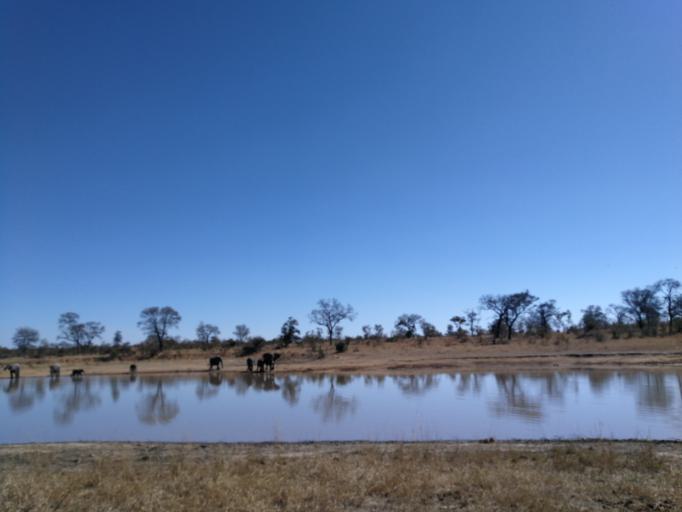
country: ZA
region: Limpopo
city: Thulamahashi
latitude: -24.8570
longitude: 31.7528
